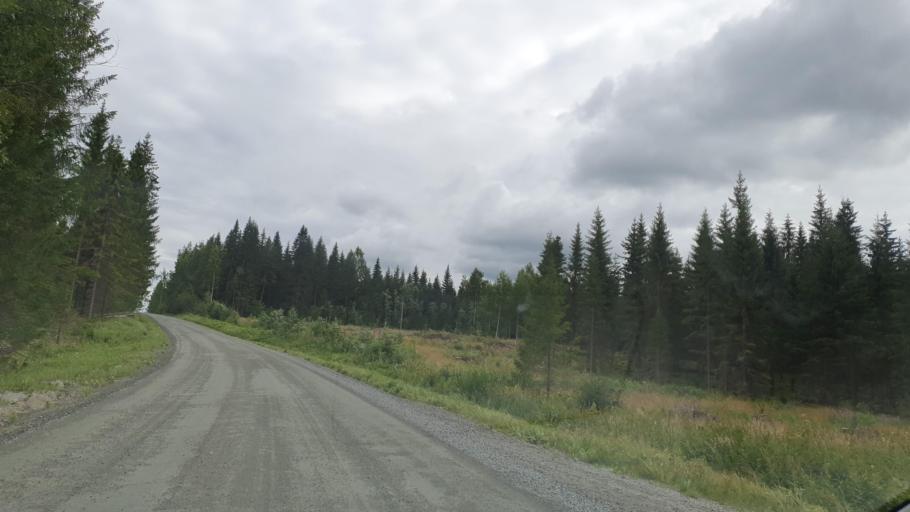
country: FI
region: Northern Savo
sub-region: Ylae-Savo
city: Iisalmi
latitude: 63.5268
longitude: 27.0892
